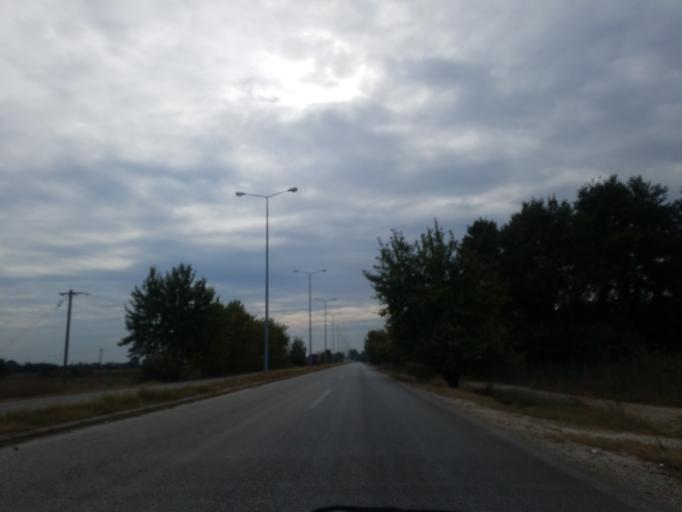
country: GR
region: Thessaly
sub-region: Trikala
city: Pyrgetos
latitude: 39.5262
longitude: 21.7484
